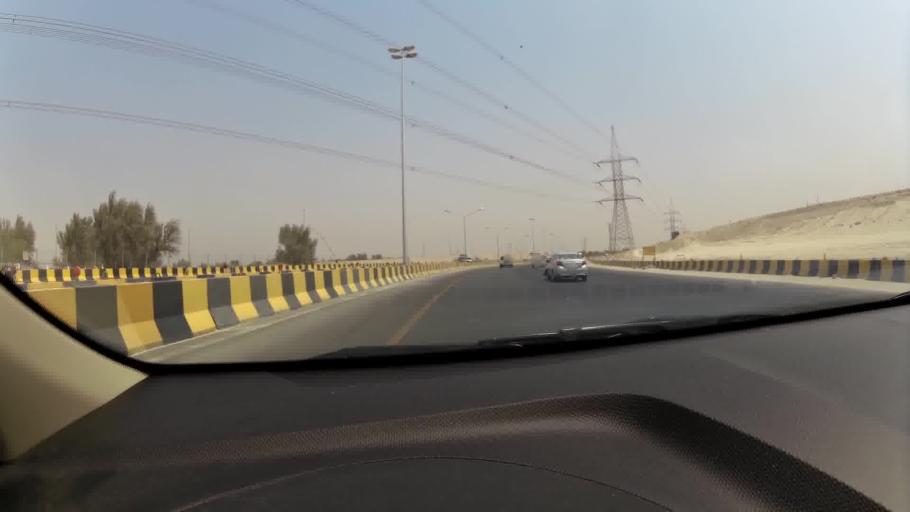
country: KW
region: Muhafazat al Jahra'
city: Al Jahra'
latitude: 29.2860
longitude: 47.7868
